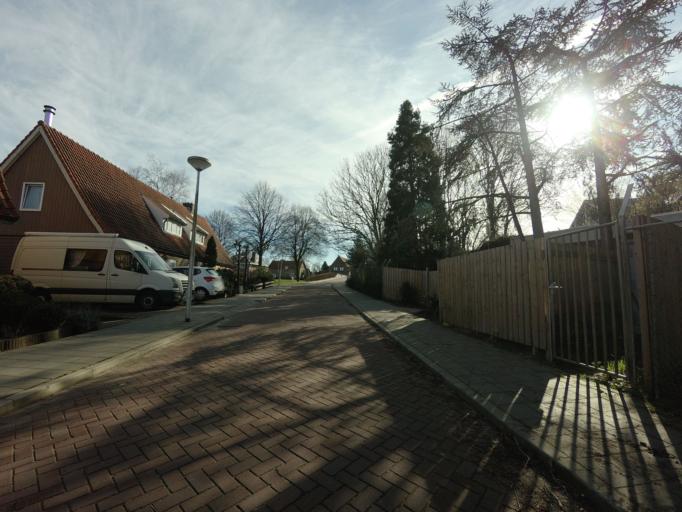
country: NL
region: South Holland
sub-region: Gemeente Kaag en Braassem
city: Oude Wetering
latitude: 52.2037
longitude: 4.6350
